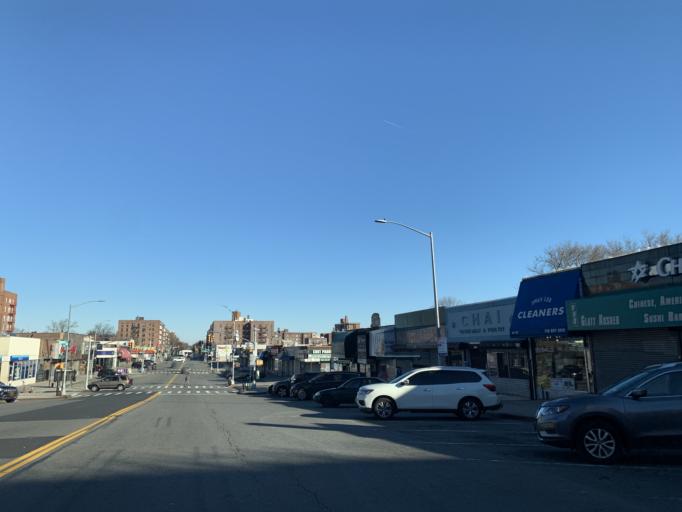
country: US
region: New York
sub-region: Queens County
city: Borough of Queens
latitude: 40.7318
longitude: -73.8489
